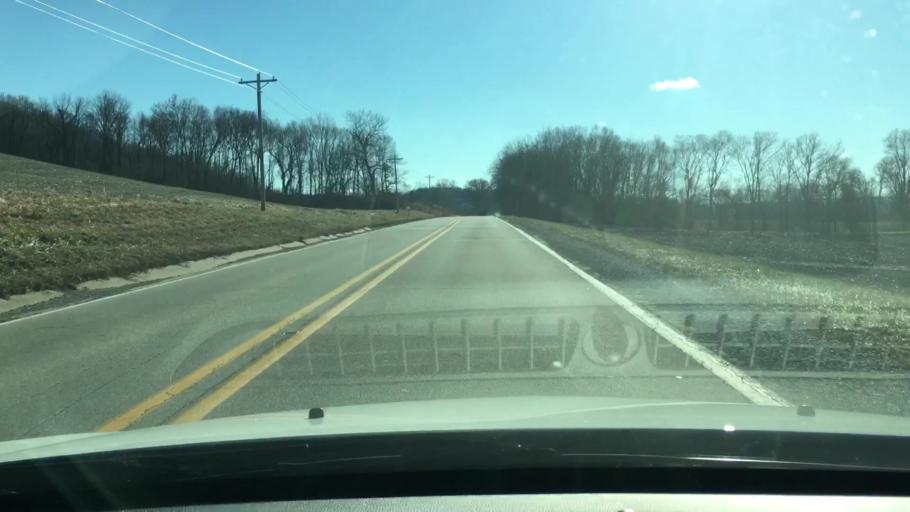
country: US
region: Illinois
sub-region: Morgan County
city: Meredosia
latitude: 39.7193
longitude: -90.5686
